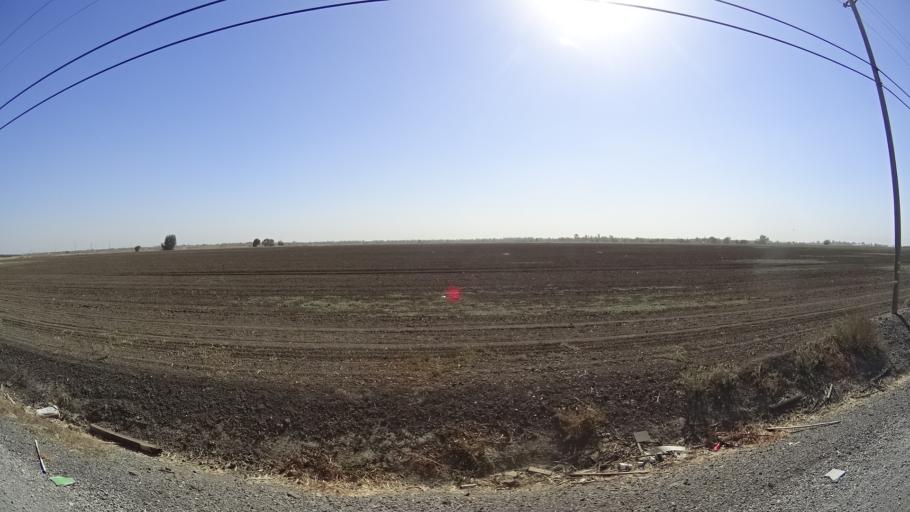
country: US
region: California
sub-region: Yolo County
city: Davis
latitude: 38.5899
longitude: -121.7428
